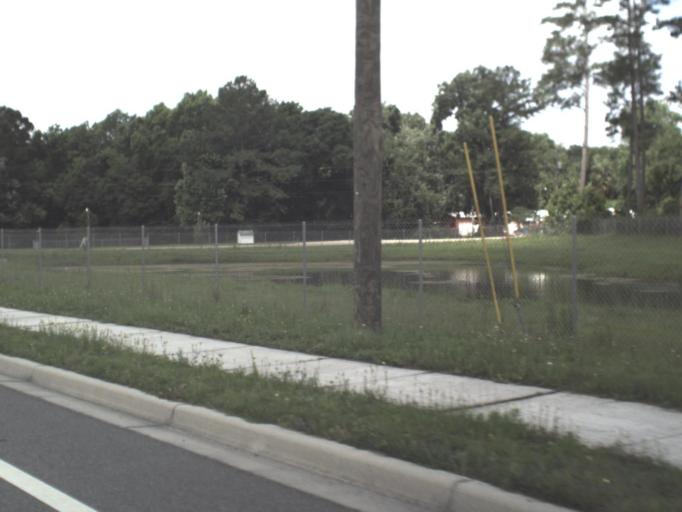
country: US
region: Florida
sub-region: Nassau County
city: Callahan
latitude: 30.5783
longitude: -81.8176
